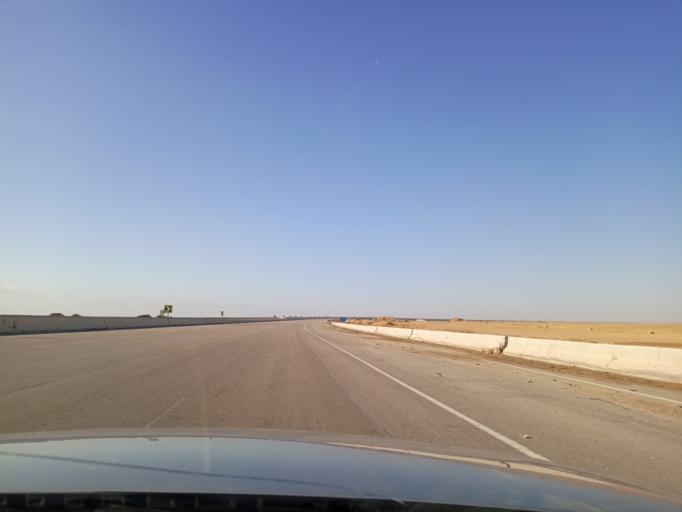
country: EG
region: Muhafazat al Fayyum
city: Tamiyah
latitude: 29.5694
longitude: 30.8366
